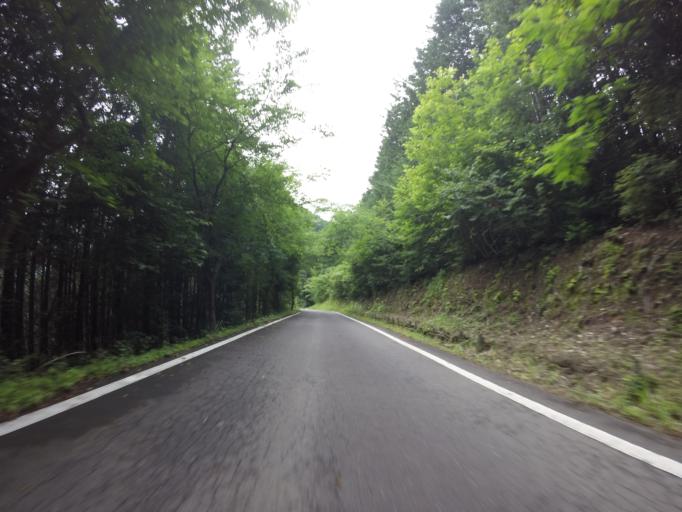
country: JP
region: Shizuoka
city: Shizuoka-shi
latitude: 35.0388
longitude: 138.3063
